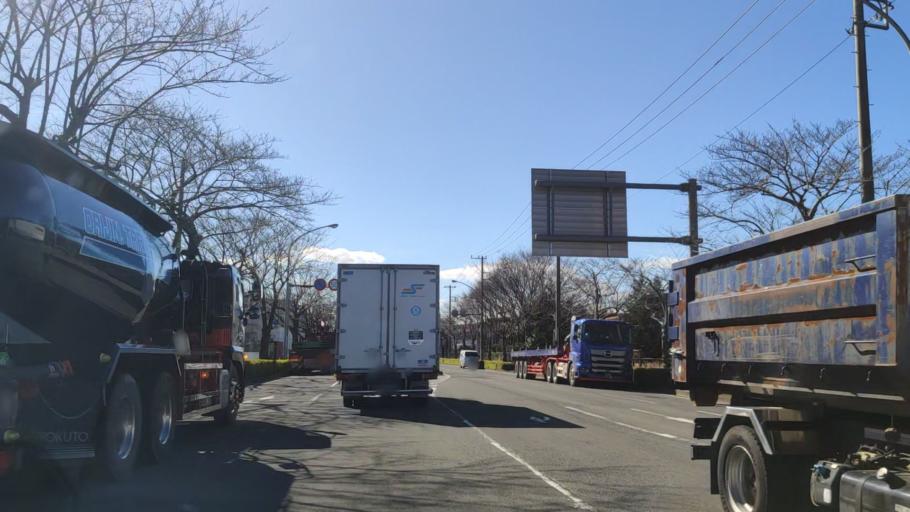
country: JP
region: Kanagawa
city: Minami-rinkan
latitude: 35.5013
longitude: 139.4851
